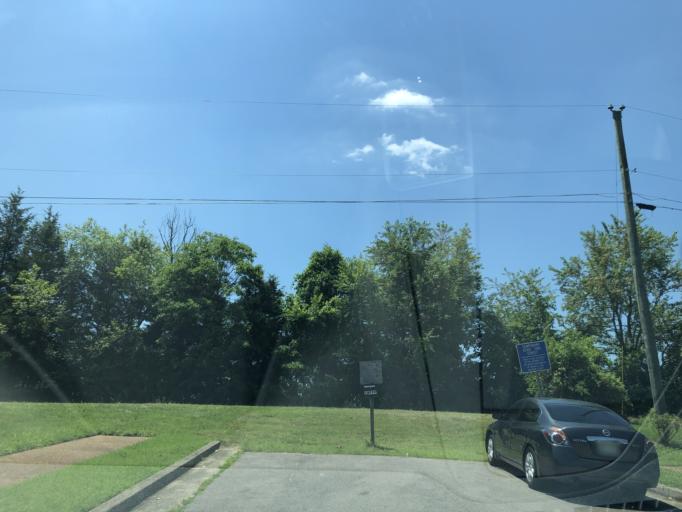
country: US
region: Tennessee
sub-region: Williamson County
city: Nolensville
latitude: 36.0152
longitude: -86.6658
